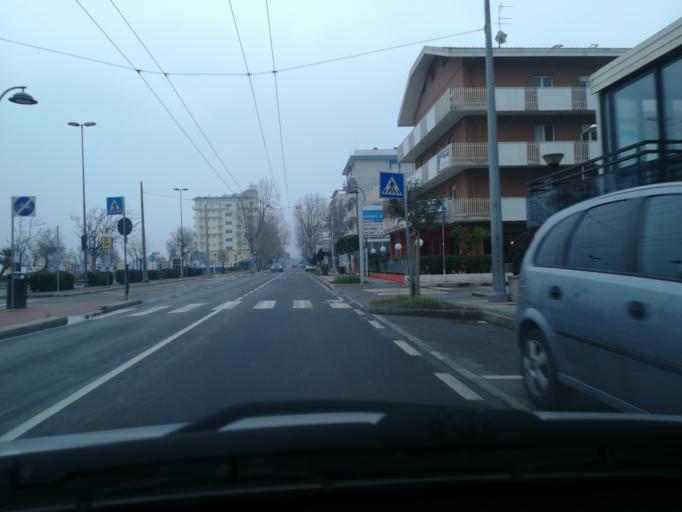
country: IT
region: Emilia-Romagna
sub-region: Provincia di Rimini
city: Riccione
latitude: 44.0168
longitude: 12.6410
